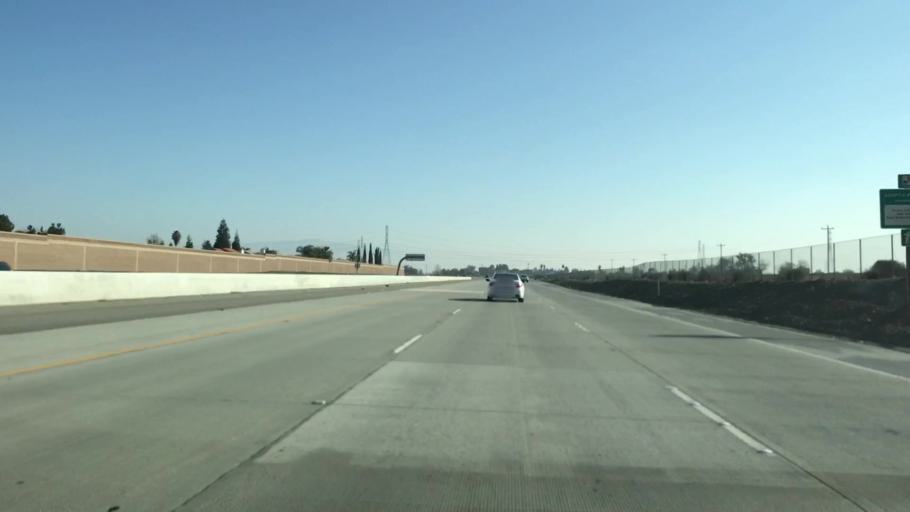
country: US
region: California
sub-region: Kern County
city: Greenacres
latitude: 35.3616
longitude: -119.1049
